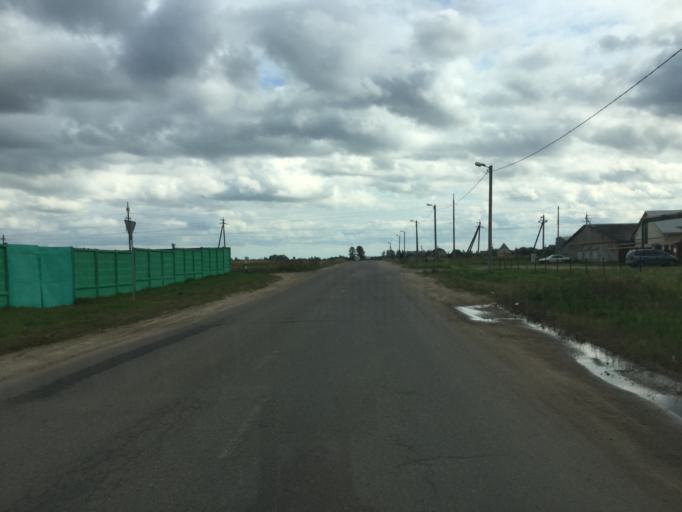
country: BY
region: Vitebsk
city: Vitebsk
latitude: 55.1584
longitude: 30.2647
